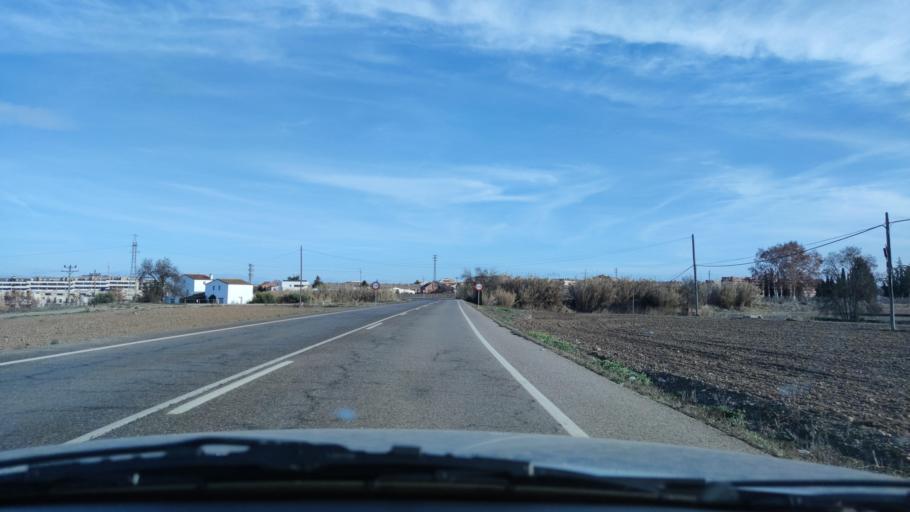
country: ES
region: Catalonia
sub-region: Provincia de Lleida
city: Lleida
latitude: 41.5957
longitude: 0.6361
